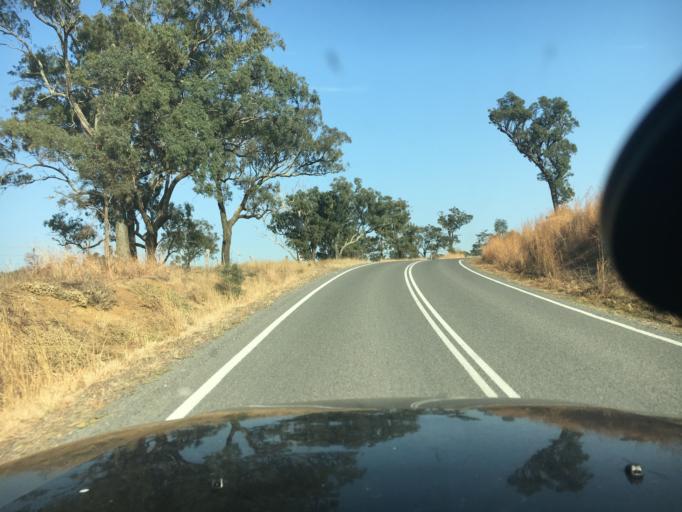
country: AU
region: New South Wales
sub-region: Cessnock
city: Branxton
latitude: -32.5920
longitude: 151.3010
